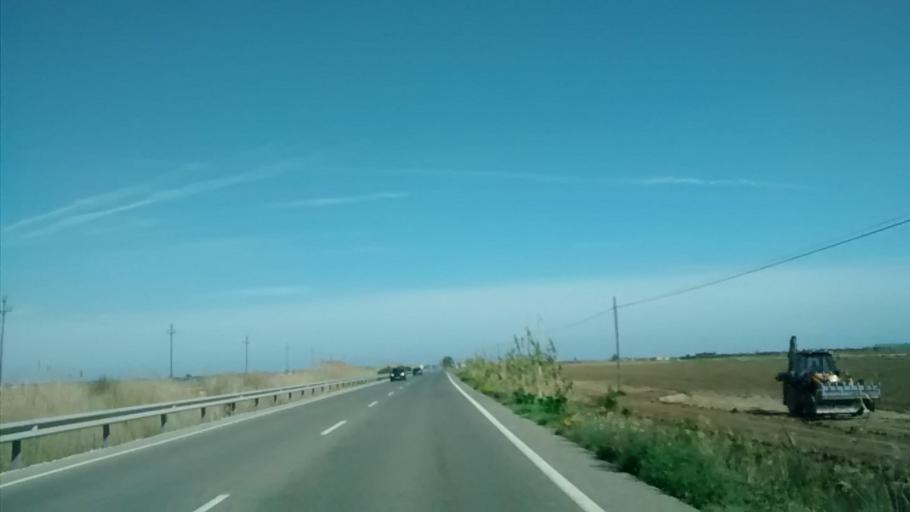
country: ES
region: Catalonia
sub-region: Provincia de Tarragona
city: Deltebre
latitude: 40.7061
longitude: 0.7720
